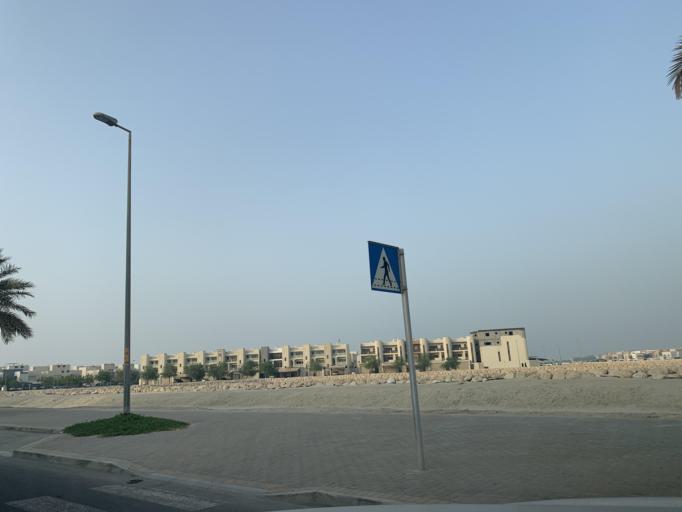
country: BH
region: Manama
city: Jidd Hafs
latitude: 26.2182
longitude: 50.4404
